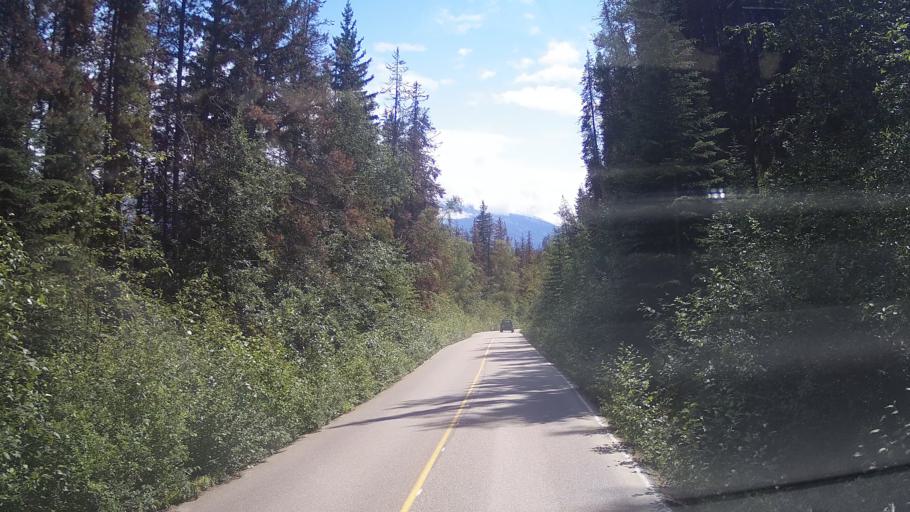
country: CA
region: Alberta
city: Jasper Park Lodge
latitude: 52.7681
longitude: -118.0286
